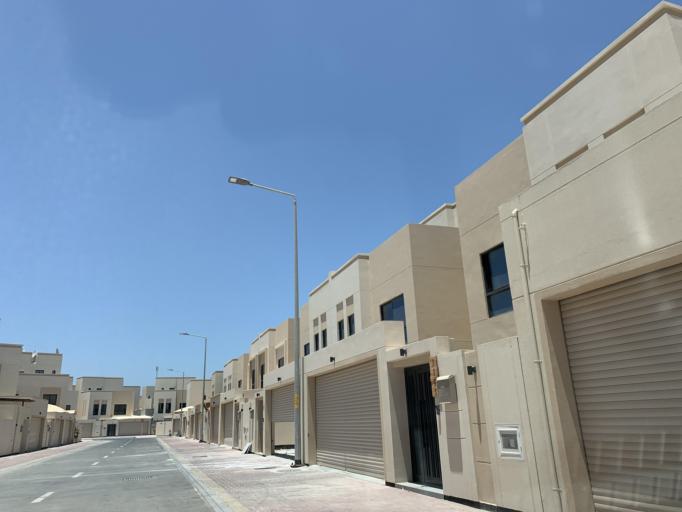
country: BH
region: Manama
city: Jidd Hafs
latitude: 26.2314
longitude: 50.4975
